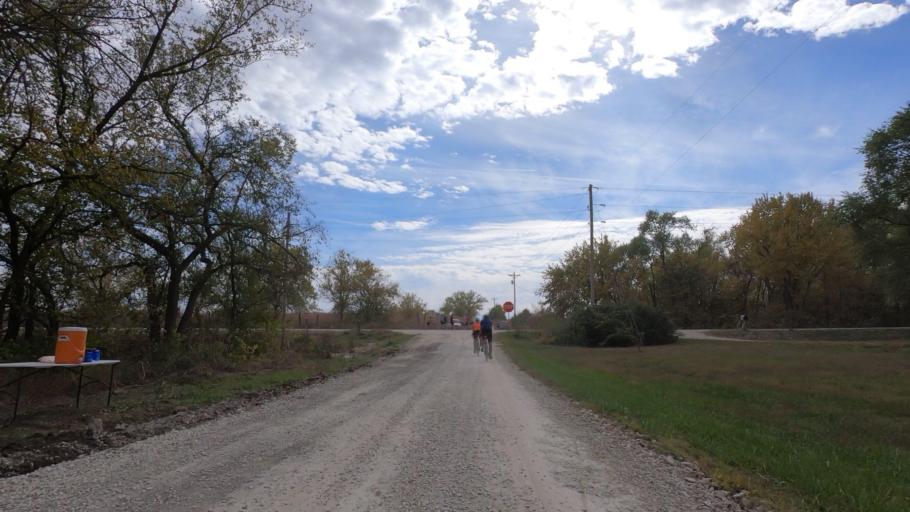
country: US
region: Kansas
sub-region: Pottawatomie County
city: Westmoreland
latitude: 39.3200
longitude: -96.4453
